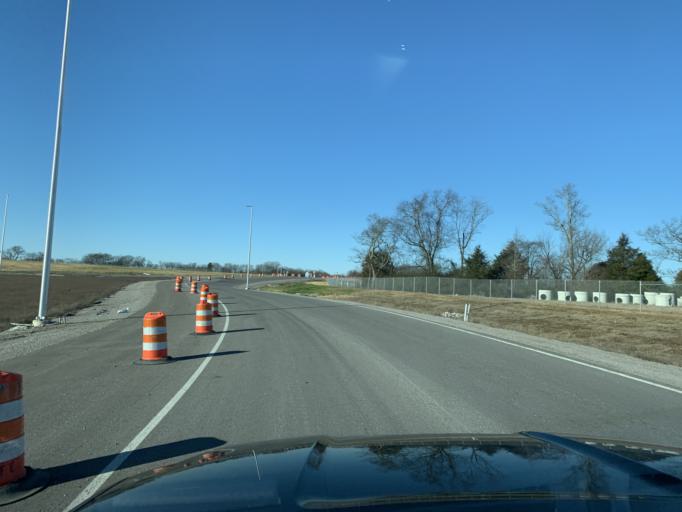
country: US
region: Tennessee
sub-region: Maury County
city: Spring Hill
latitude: 35.7471
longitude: -86.9487
